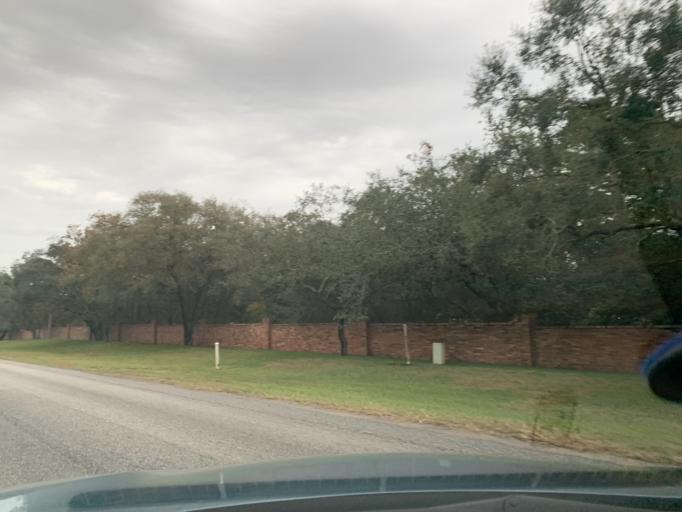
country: US
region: Florida
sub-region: Hernando County
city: Timber Pines
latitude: 28.4339
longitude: -82.5851
